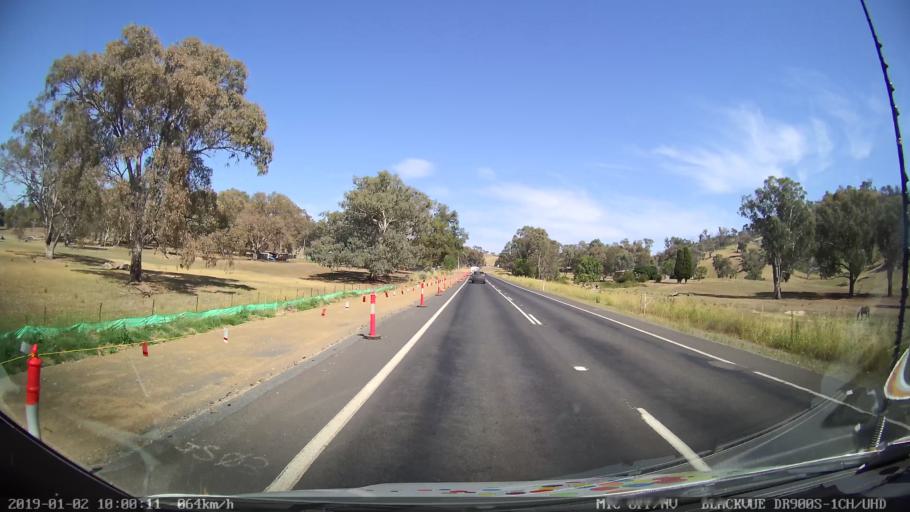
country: AU
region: New South Wales
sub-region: Gundagai
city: Gundagai
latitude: -35.1961
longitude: 148.1344
